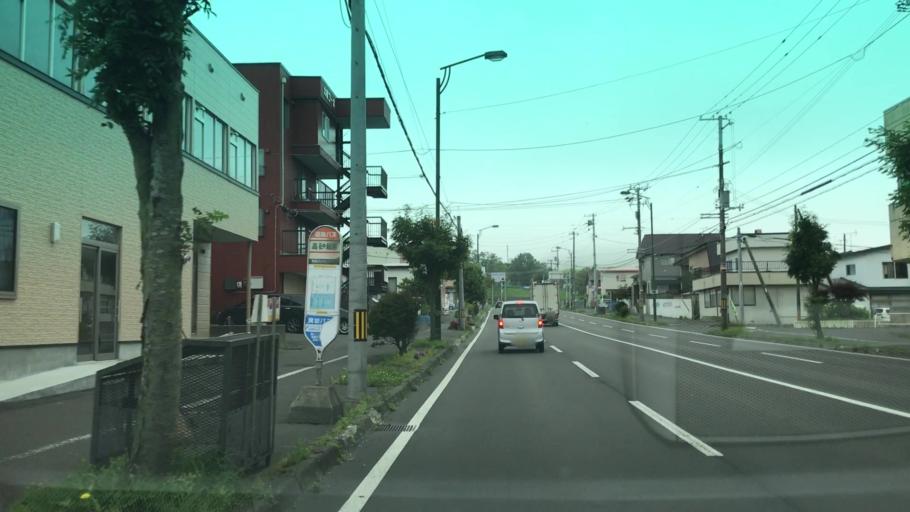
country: JP
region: Hokkaido
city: Muroran
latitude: 42.3638
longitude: 141.0382
